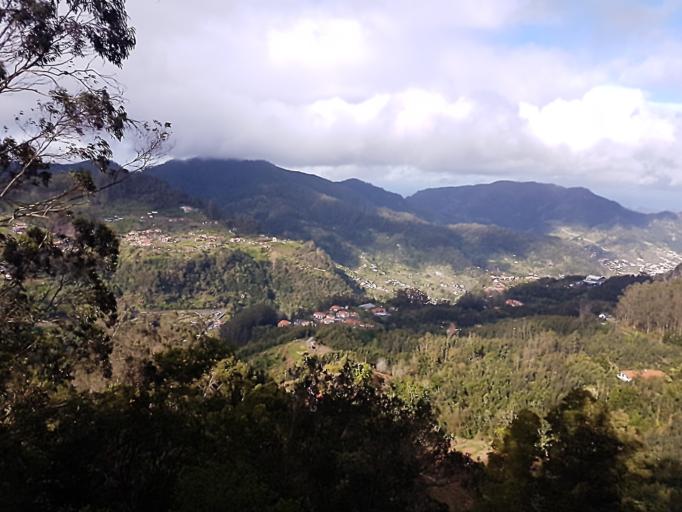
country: PT
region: Madeira
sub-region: Santa Cruz
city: Santa Cruz
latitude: 32.7277
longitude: -16.8163
